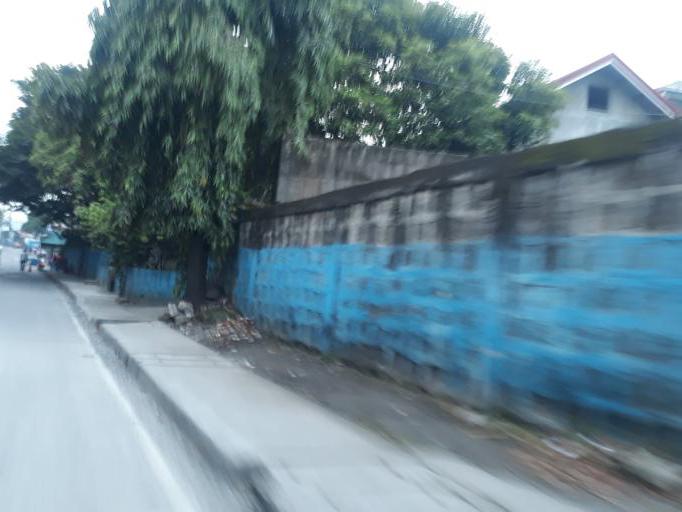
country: PH
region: Calabarzon
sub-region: Province of Rizal
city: Valenzuela
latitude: 14.6967
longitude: 120.9595
